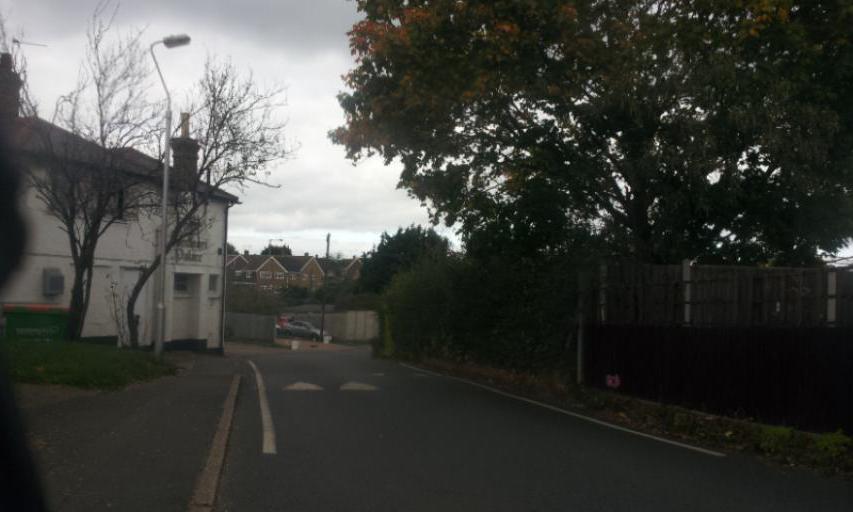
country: GB
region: England
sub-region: Kent
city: Larkfield
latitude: 51.2984
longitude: 0.4468
